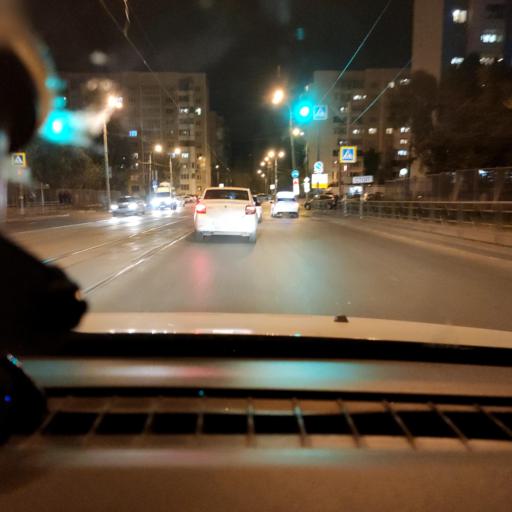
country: RU
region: Samara
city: Samara
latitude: 53.1899
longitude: 50.1394
